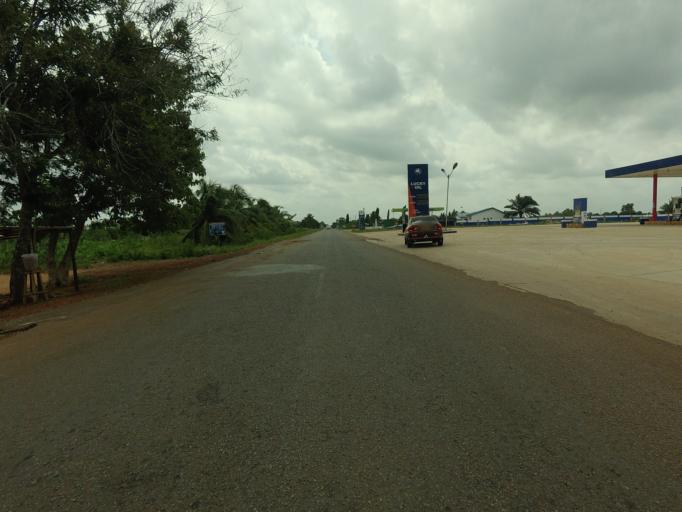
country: TG
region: Maritime
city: Lome
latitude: 6.1356
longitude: 1.1170
